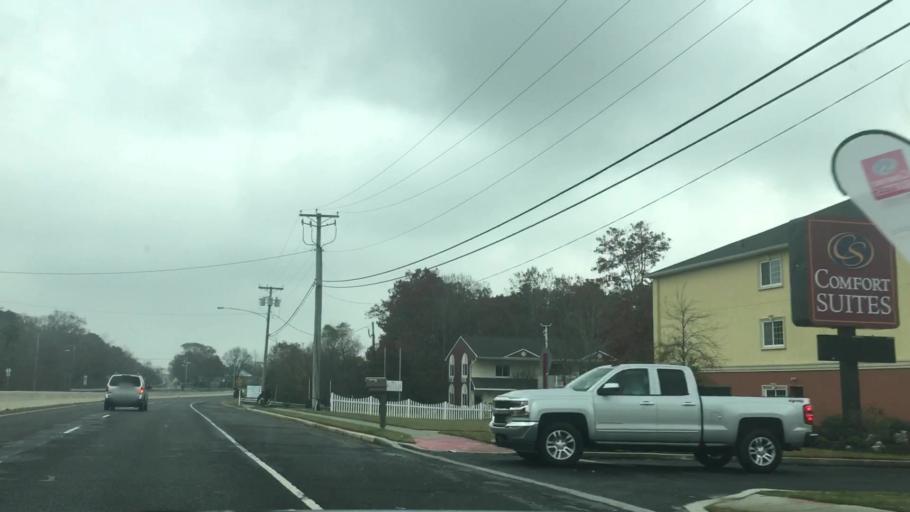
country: US
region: New Jersey
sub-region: Atlantic County
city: Absecon
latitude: 39.4402
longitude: -74.5200
